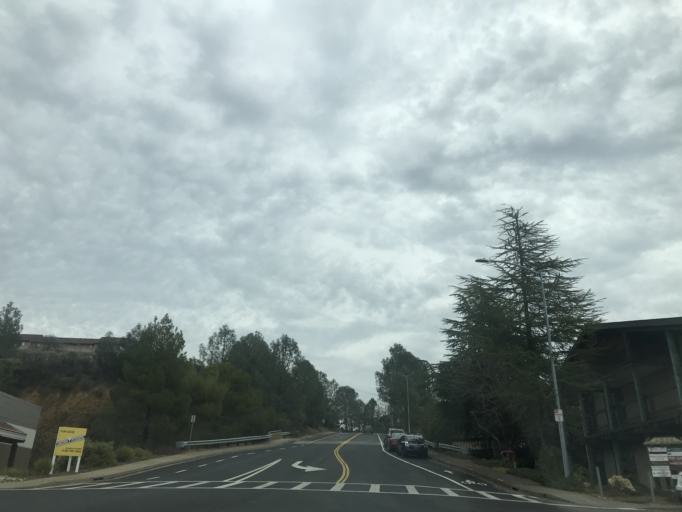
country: US
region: California
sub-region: El Dorado County
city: Placerville
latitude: 38.7283
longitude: -120.8362
